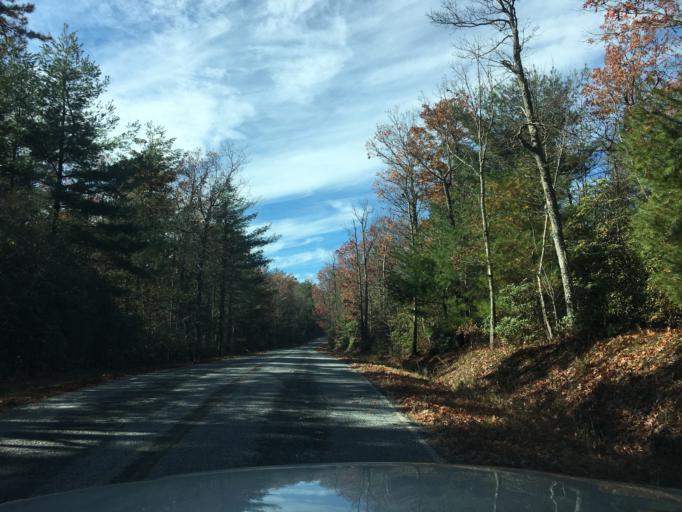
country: US
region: North Carolina
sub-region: Henderson County
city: Valley Hill
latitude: 35.2335
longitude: -82.5168
